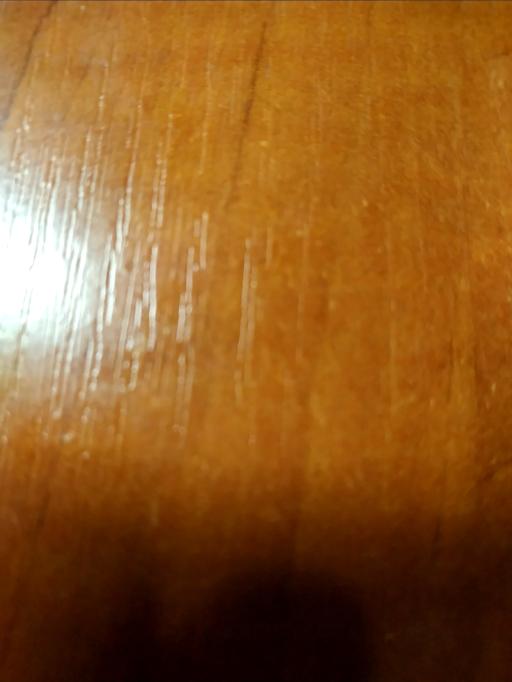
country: RU
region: Moskovskaya
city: Zaraysk
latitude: 54.5233
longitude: 39.0007
